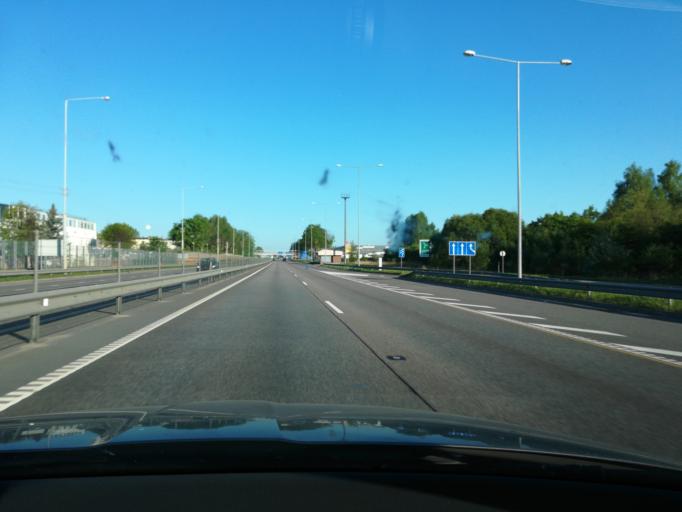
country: LT
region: Vilnius County
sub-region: Vilniaus Rajonas
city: Vievis
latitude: 54.7729
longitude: 24.8165
